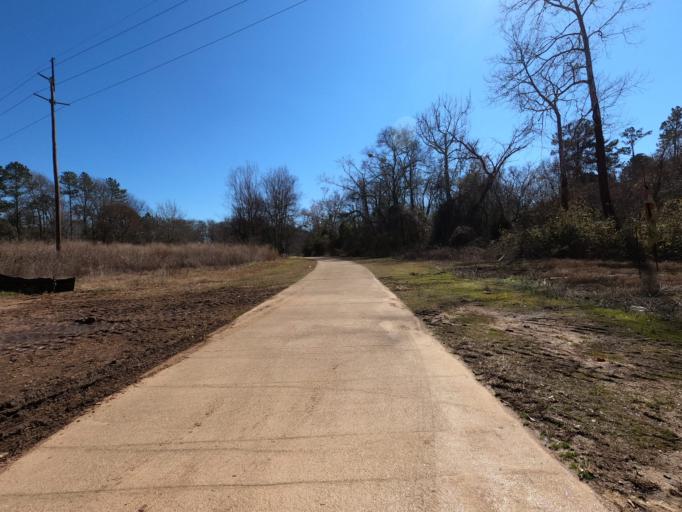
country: US
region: Georgia
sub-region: Clarke County
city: Athens
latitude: 33.9738
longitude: -83.3811
